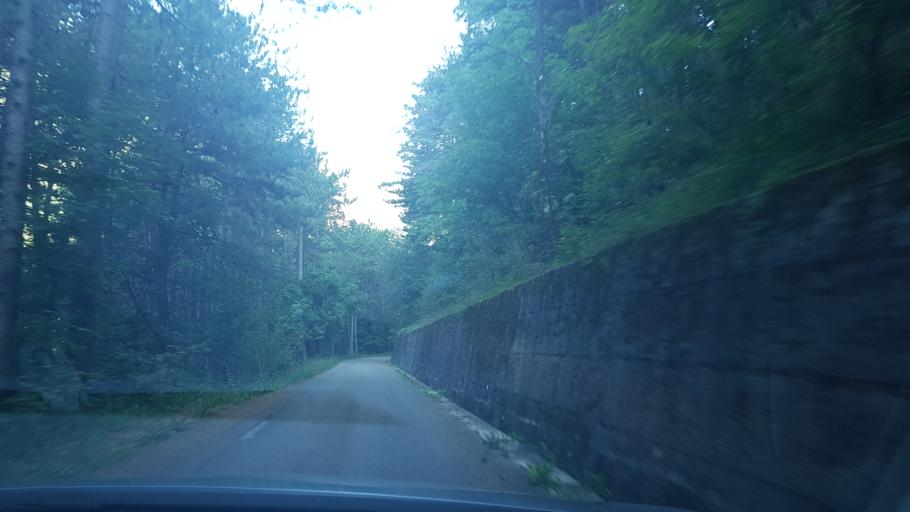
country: IT
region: Friuli Venezia Giulia
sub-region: Provincia di Udine
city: Moggio Udinese
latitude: 46.4312
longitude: 13.2062
